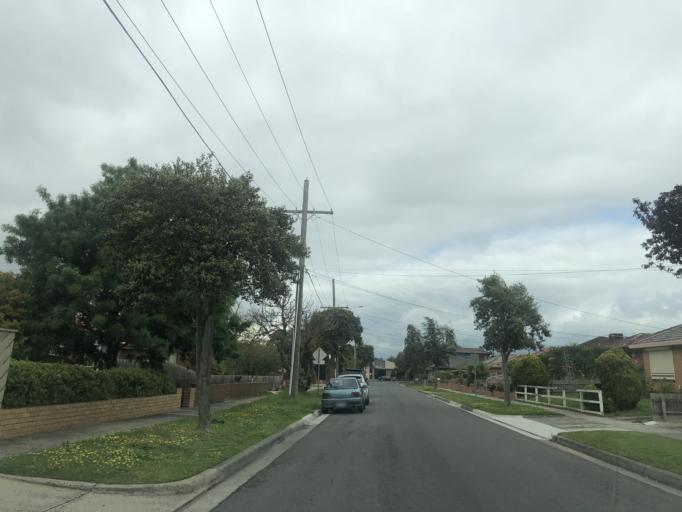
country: AU
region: Victoria
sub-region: Greater Dandenong
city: Dandenong North
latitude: -37.9683
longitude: 145.2125
